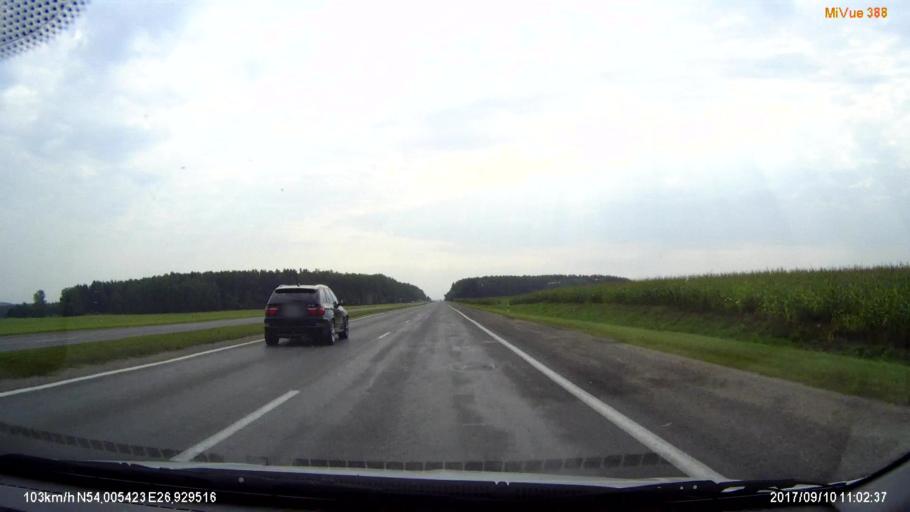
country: BY
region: Minsk
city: Rakaw
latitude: 54.0054
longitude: 26.9295
